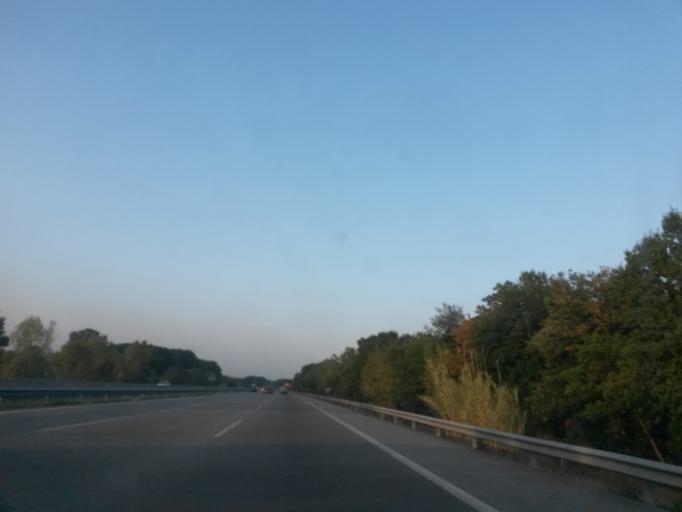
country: ES
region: Catalonia
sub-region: Provincia de Girona
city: Breda
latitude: 41.7181
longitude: 2.5666
